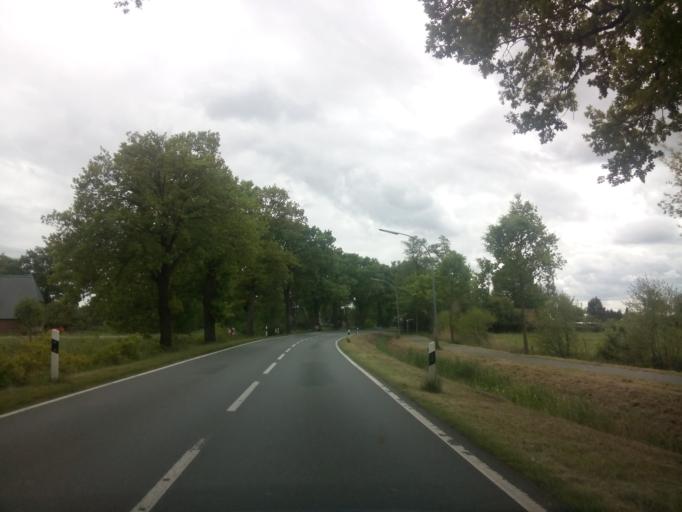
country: DE
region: Lower Saxony
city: Delmenhorst
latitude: 53.1064
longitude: 8.6461
